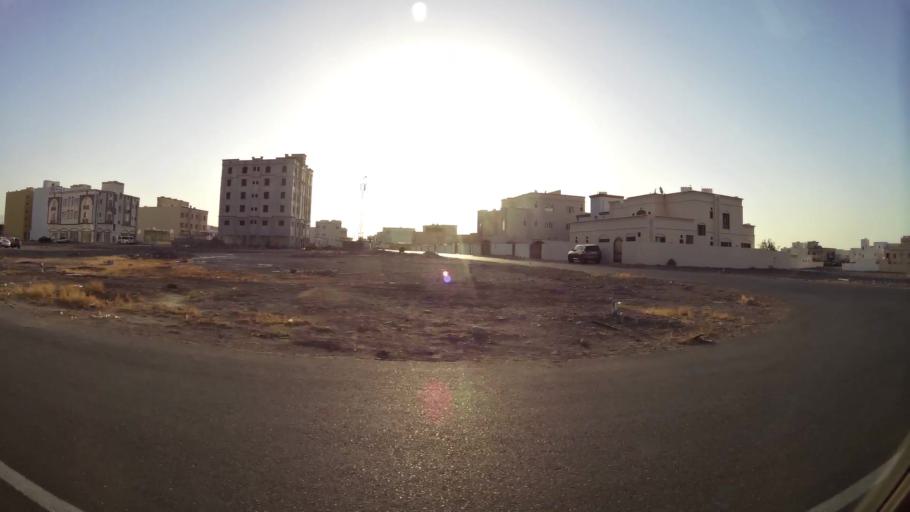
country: OM
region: Muhafazat Masqat
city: As Sib al Jadidah
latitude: 23.5915
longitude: 58.1353
